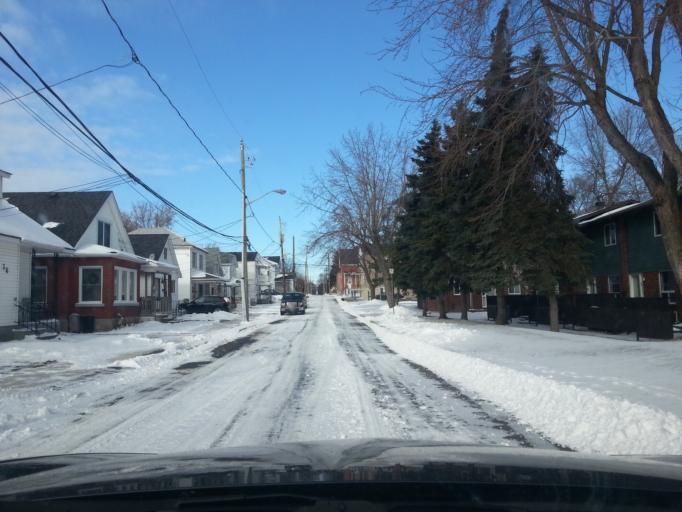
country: CA
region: Ontario
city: Cornwall
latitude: 45.0165
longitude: -74.7180
